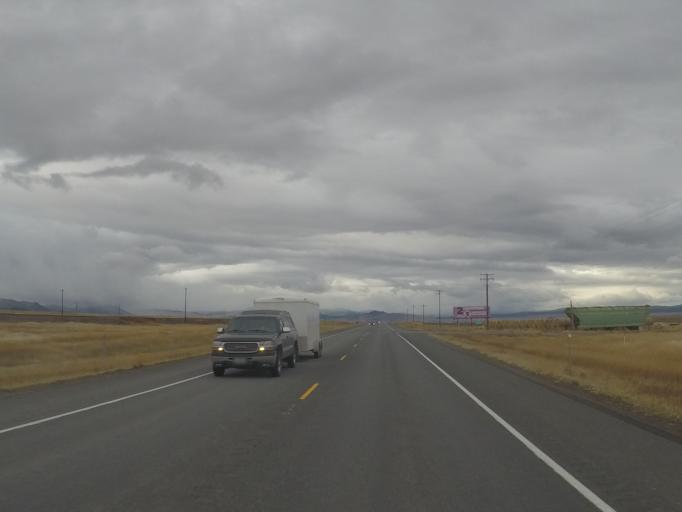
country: US
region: Montana
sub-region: Lewis and Clark County
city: East Helena
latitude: 46.5725
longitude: -111.8272
